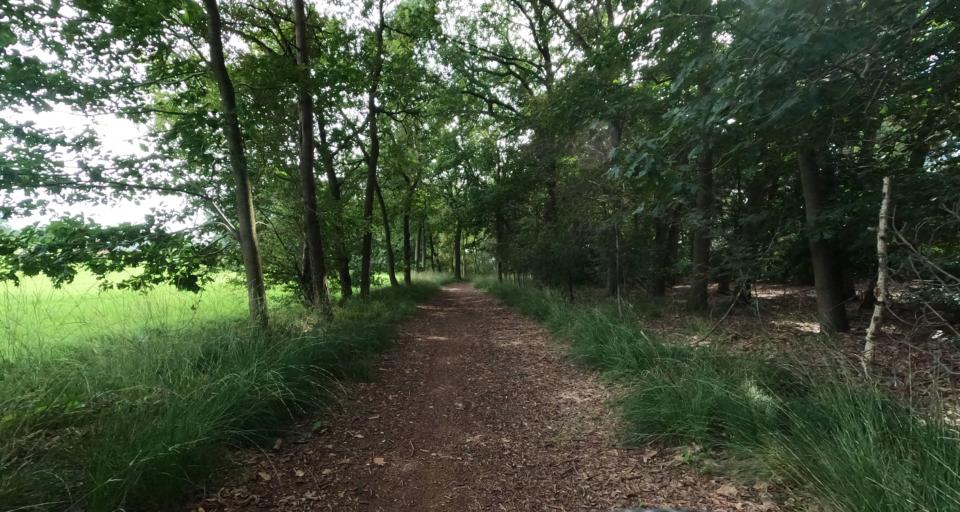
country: BE
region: Flanders
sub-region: Provincie Antwerpen
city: Kalmthout
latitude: 51.4050
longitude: 4.4642
